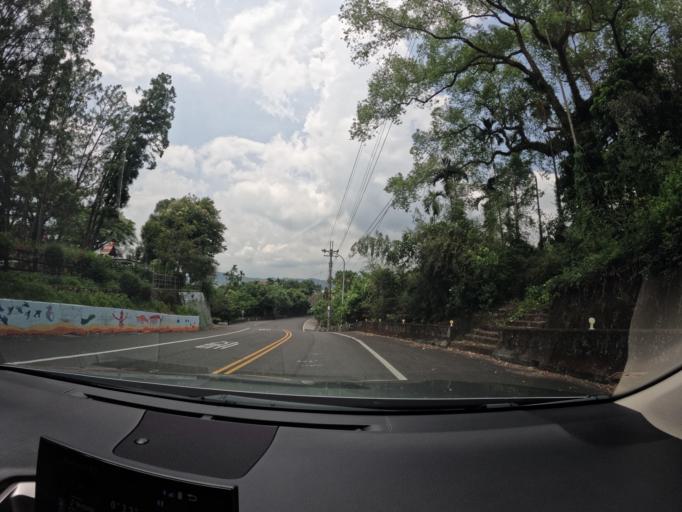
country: TW
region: Taiwan
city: Lugu
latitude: 23.8023
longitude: 120.7900
